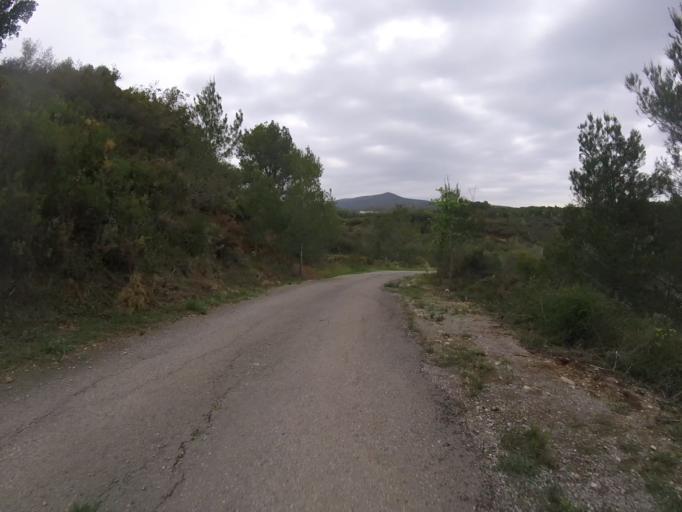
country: ES
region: Valencia
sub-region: Provincia de Castello
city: Cuevas de Vinroma
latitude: 40.2917
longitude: 0.0857
